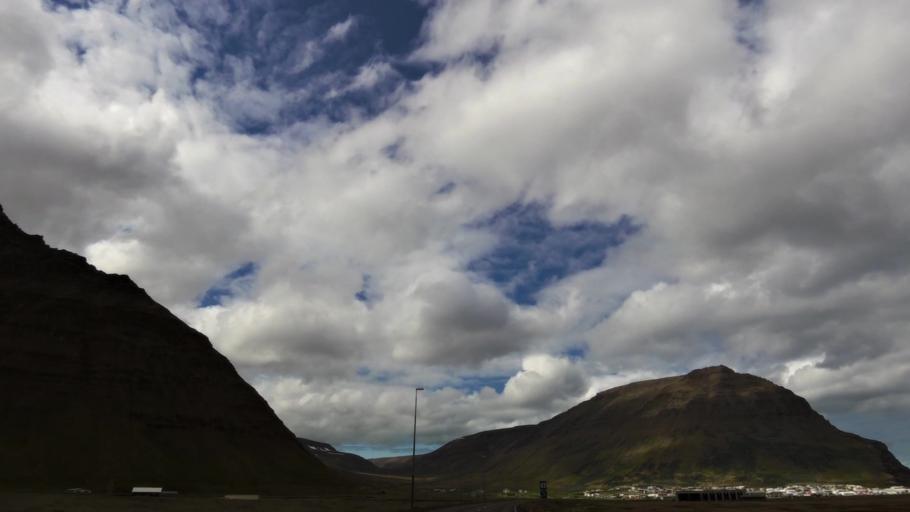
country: IS
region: Westfjords
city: Isafjoerdur
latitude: 66.1457
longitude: -23.2365
